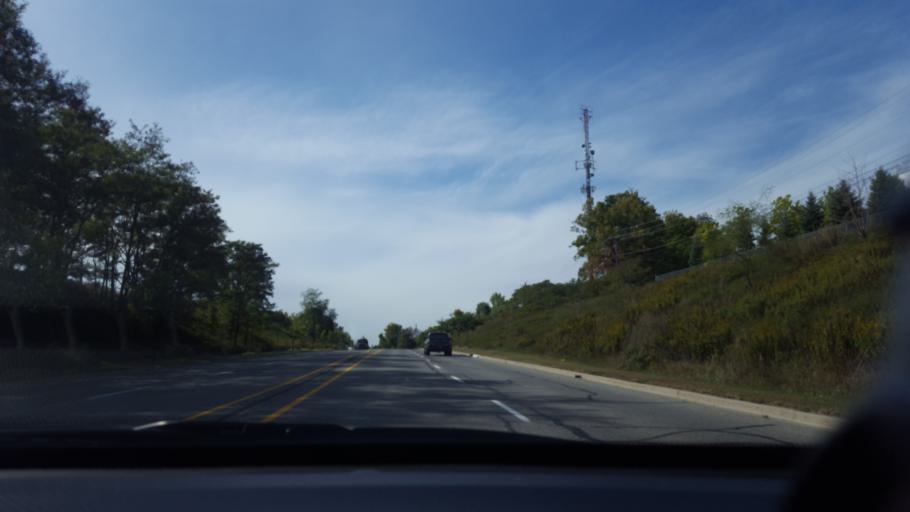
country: CA
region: Ontario
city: Newmarket
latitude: 44.0242
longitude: -79.4977
